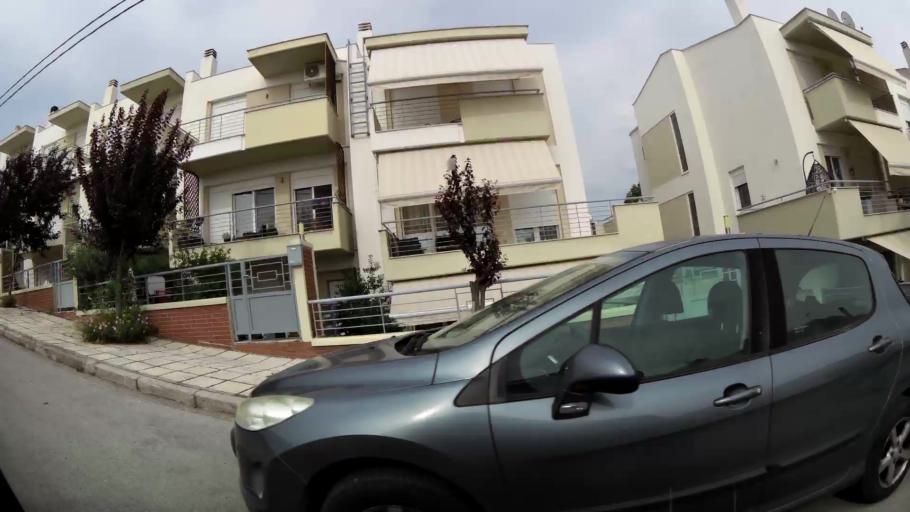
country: GR
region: Central Macedonia
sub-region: Nomos Thessalonikis
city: Oraiokastro
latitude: 40.7291
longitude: 22.9252
